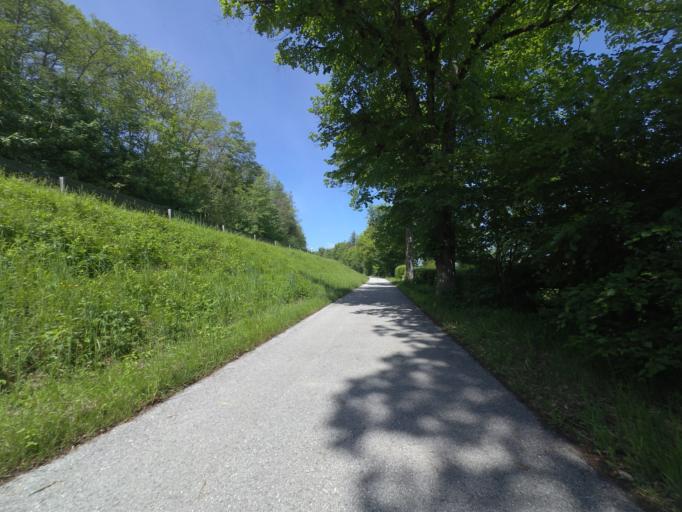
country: DE
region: Bavaria
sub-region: Upper Bavaria
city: Waging am See
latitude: 47.9337
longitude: 12.7716
